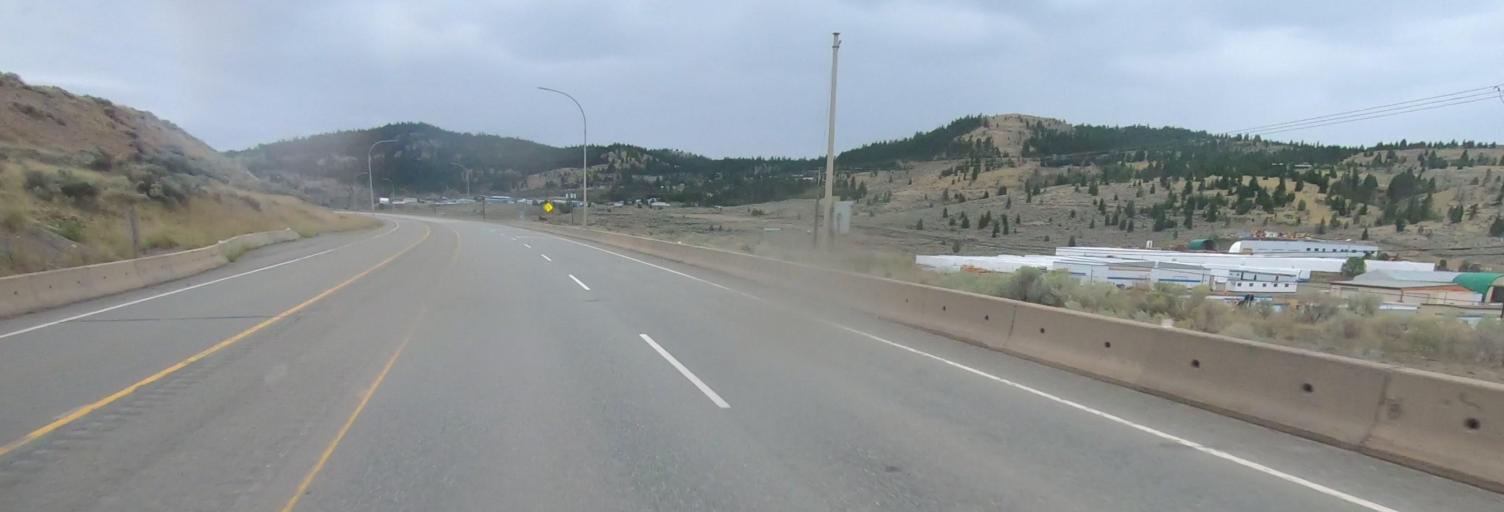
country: CA
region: British Columbia
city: Kamloops
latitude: 50.6628
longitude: -120.4541
